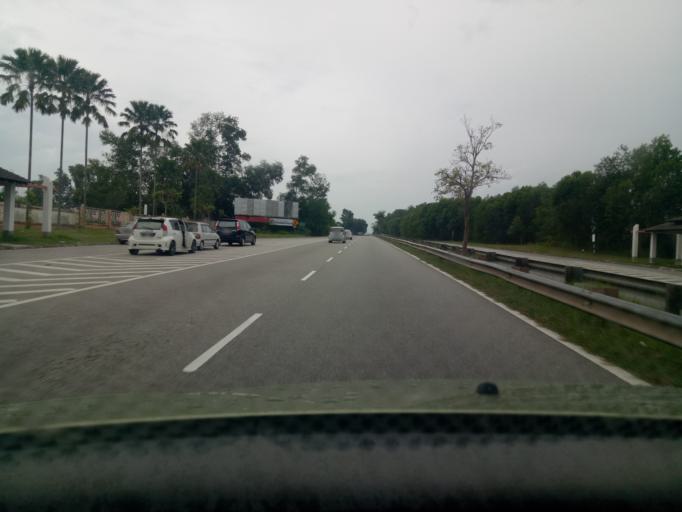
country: MY
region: Kedah
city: Sungai Petani
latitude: 5.6681
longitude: 100.5175
